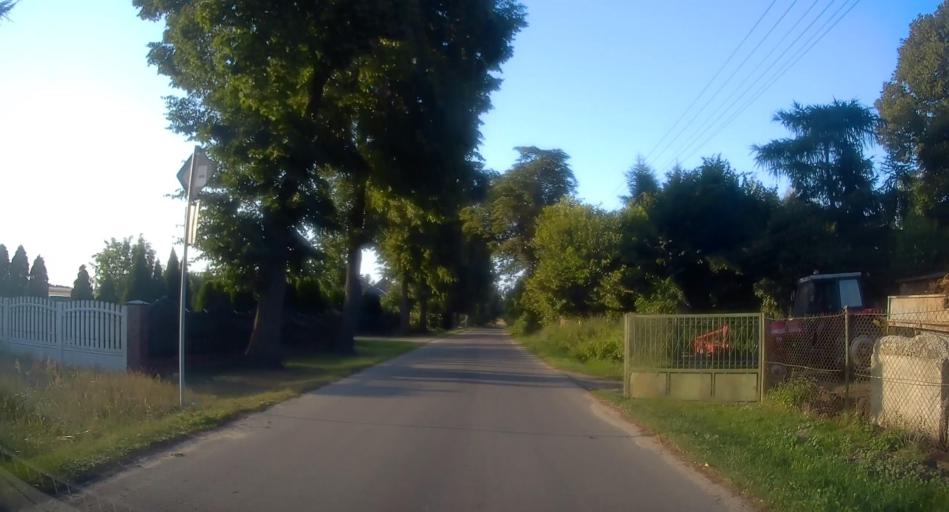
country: PL
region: Lodz Voivodeship
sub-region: Powiat skierniewicki
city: Kaweczyn Nowy
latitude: 51.8819
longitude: 20.2790
